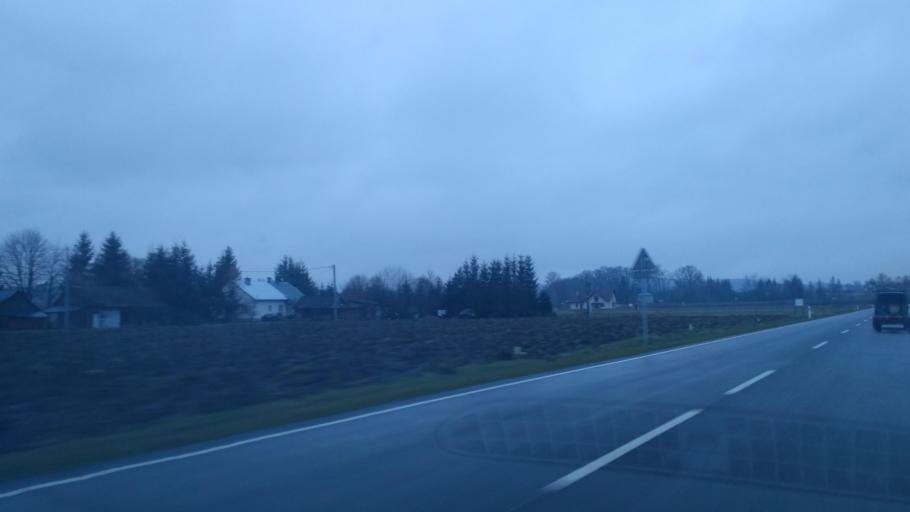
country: PL
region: Subcarpathian Voivodeship
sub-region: Powiat rzeszowski
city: Dynow
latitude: 49.8303
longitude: 22.2415
